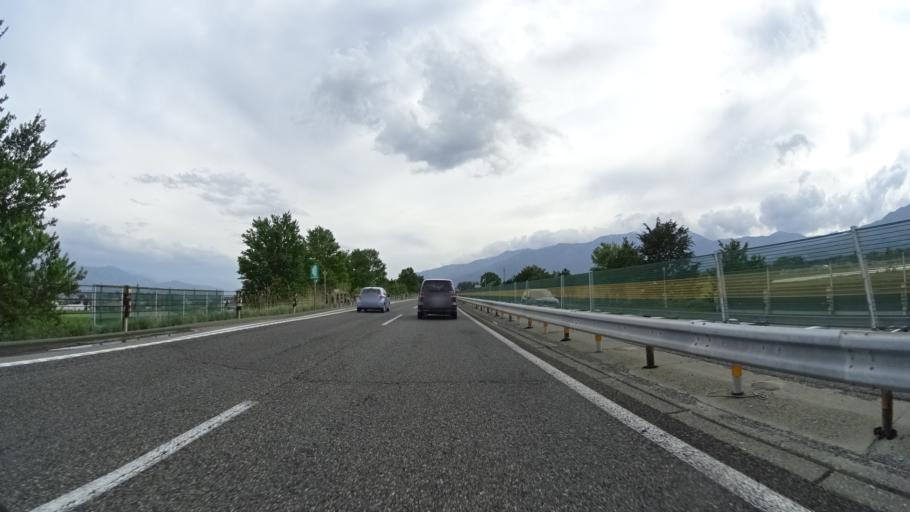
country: JP
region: Nagano
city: Ina
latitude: 35.8893
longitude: 137.9582
